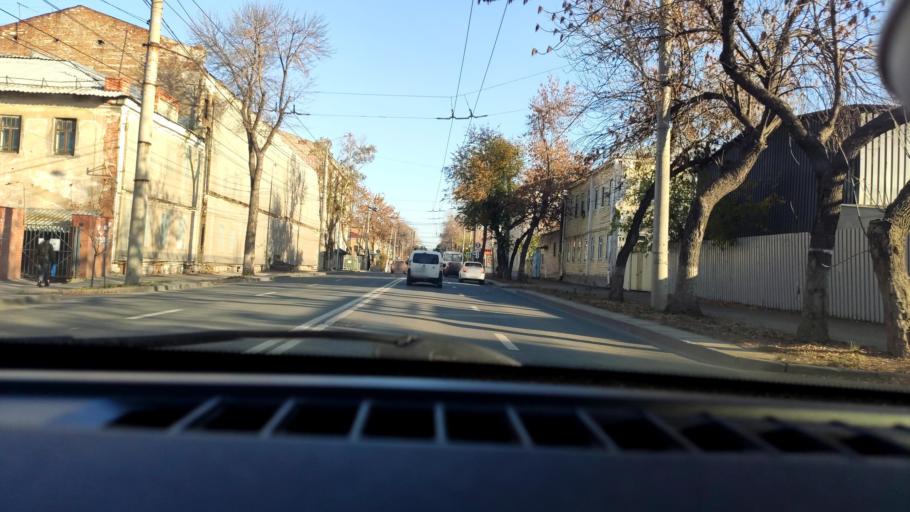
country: RU
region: Samara
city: Rozhdestveno
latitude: 53.1790
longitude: 50.0759
